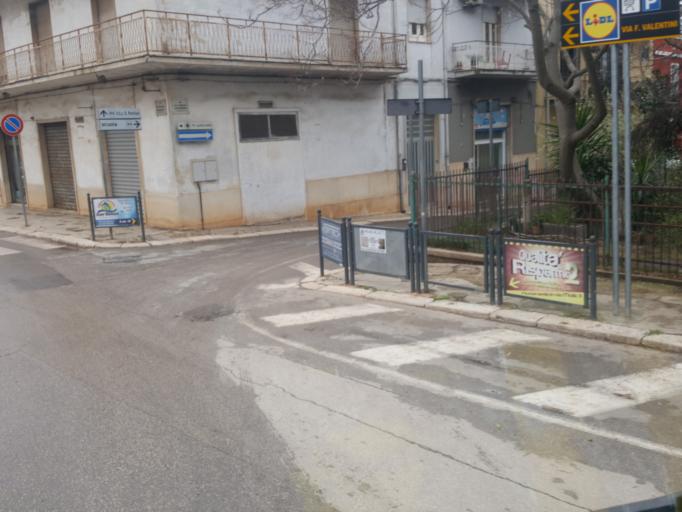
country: IT
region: Apulia
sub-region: Provincia di Bari
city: Turi
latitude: 40.9174
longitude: 17.0226
